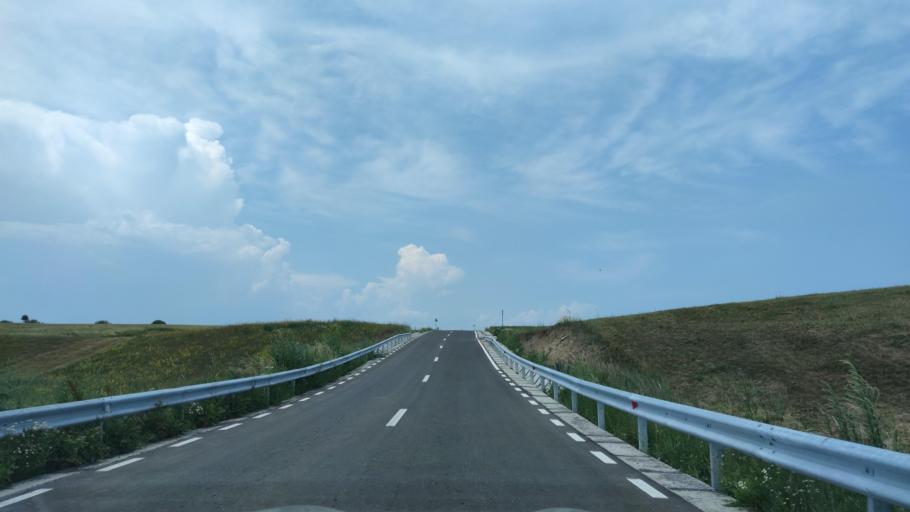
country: RO
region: Harghita
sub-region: Comuna Subcetate
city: Subcetate
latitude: 46.8211
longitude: 25.4471
